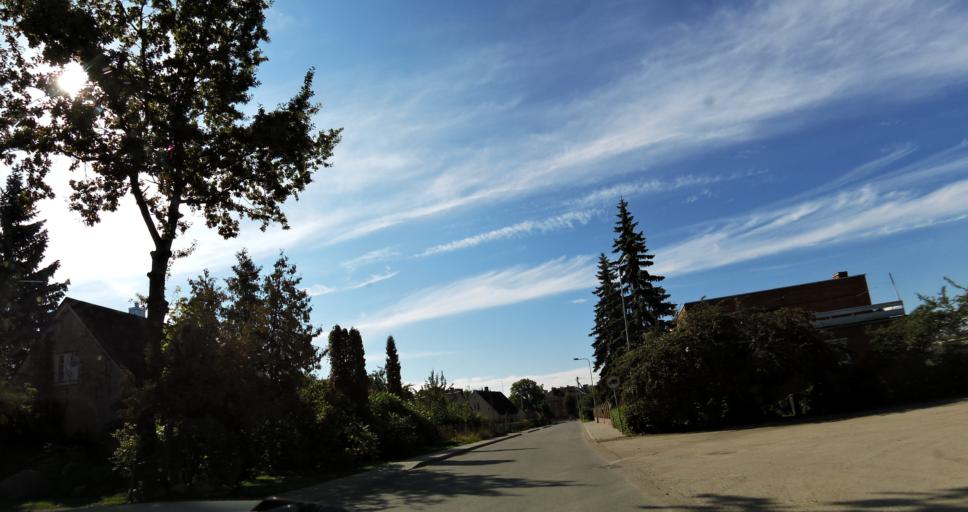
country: LT
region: Panevezys
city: Pasvalys
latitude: 56.0646
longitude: 24.3965
